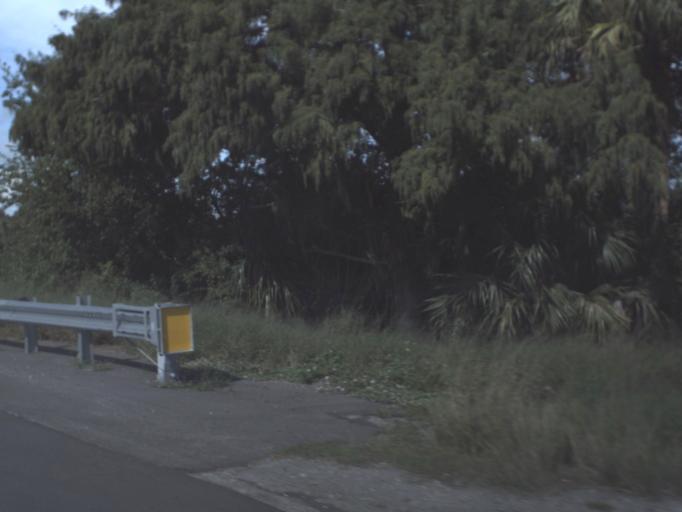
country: US
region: Florida
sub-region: Glades County
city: Buckhead Ridge
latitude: 27.1467
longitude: -80.8741
